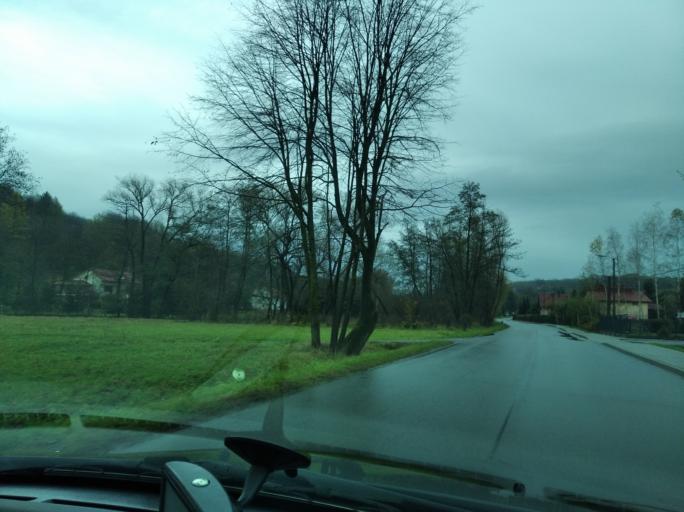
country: PL
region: Subcarpathian Voivodeship
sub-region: Powiat rzeszowski
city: Straszydle
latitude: 49.9086
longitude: 21.9621
